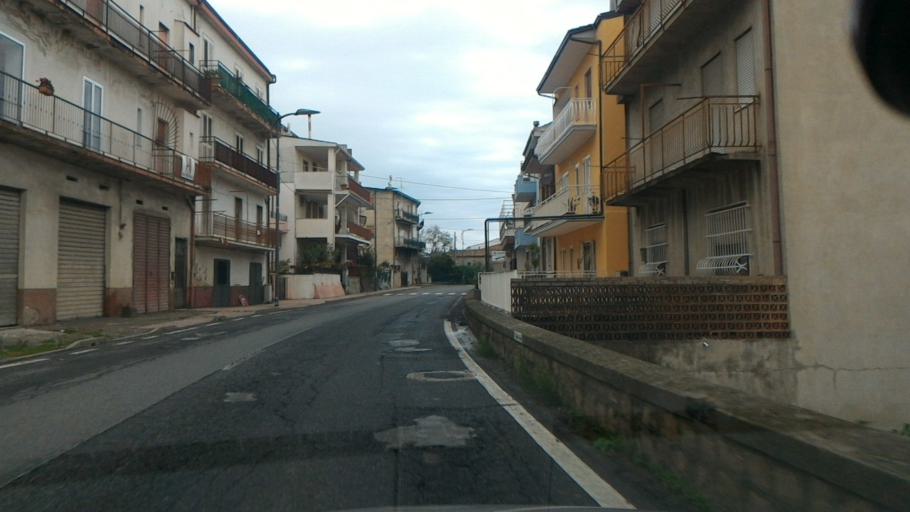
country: IT
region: Calabria
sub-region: Provincia di Crotone
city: Torretta
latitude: 39.4475
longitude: 17.0415
